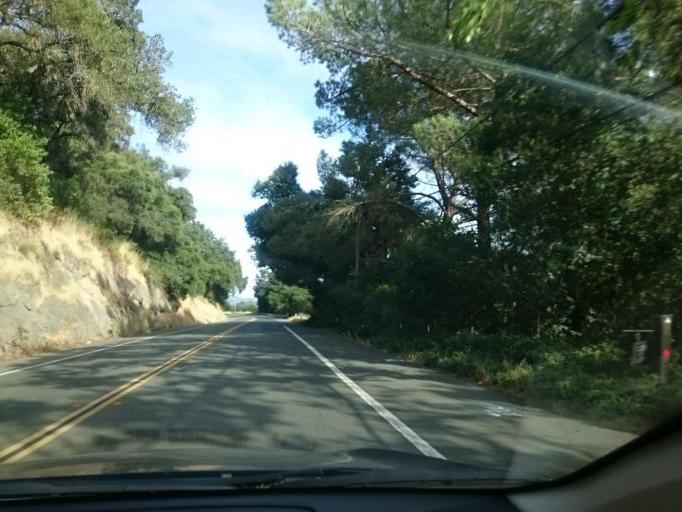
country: US
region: California
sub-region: Napa County
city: Saint Helena
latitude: 38.5001
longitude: -122.4301
